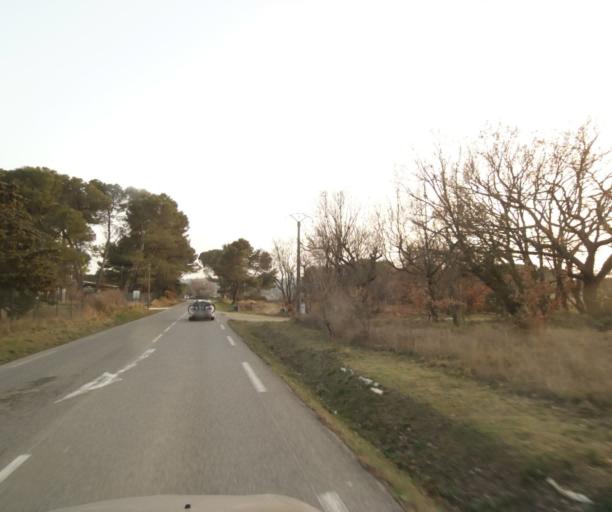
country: FR
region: Provence-Alpes-Cote d'Azur
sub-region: Departement des Bouches-du-Rhone
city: Eguilles
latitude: 43.5946
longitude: 5.3665
